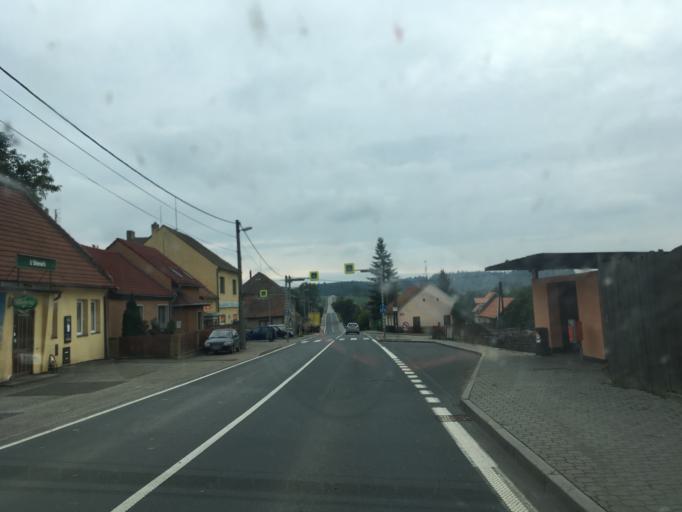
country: CZ
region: Vysocina
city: Namest' nad Oslavou
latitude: 49.1976
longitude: 16.2024
